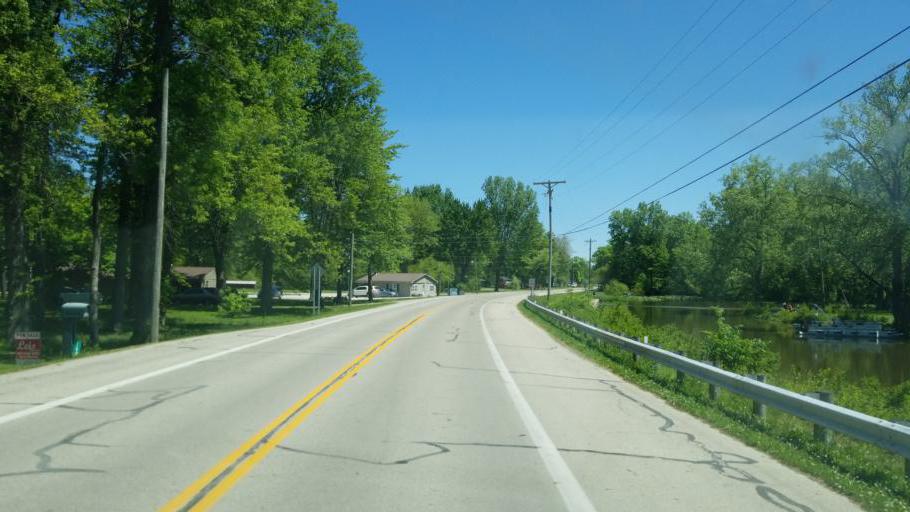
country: US
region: Ohio
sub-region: Shelby County
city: Fort Loramie
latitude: 40.3707
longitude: -84.3647
